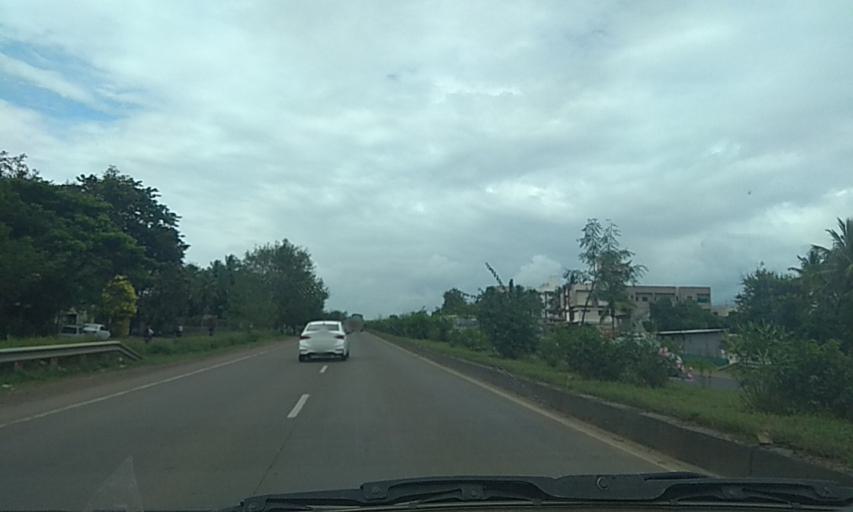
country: IN
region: Maharashtra
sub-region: Kolhapur
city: Kagal
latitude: 16.5869
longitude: 74.3090
